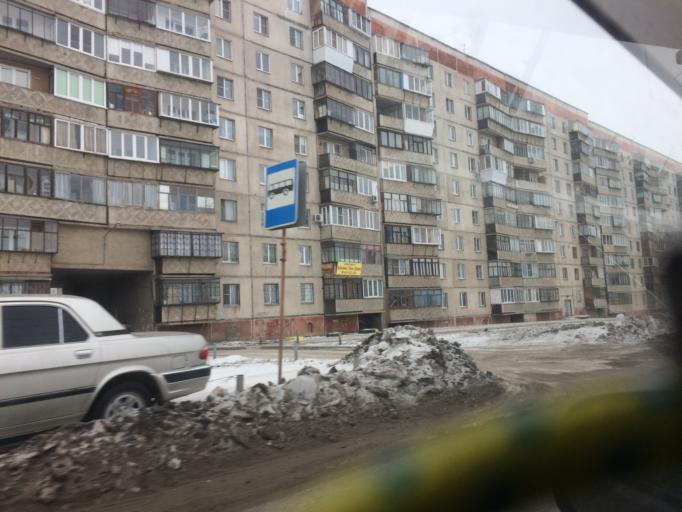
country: RU
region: Chelyabinsk
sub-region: Gorod Magnitogorsk
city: Magnitogorsk
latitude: 53.3610
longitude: 58.9876
